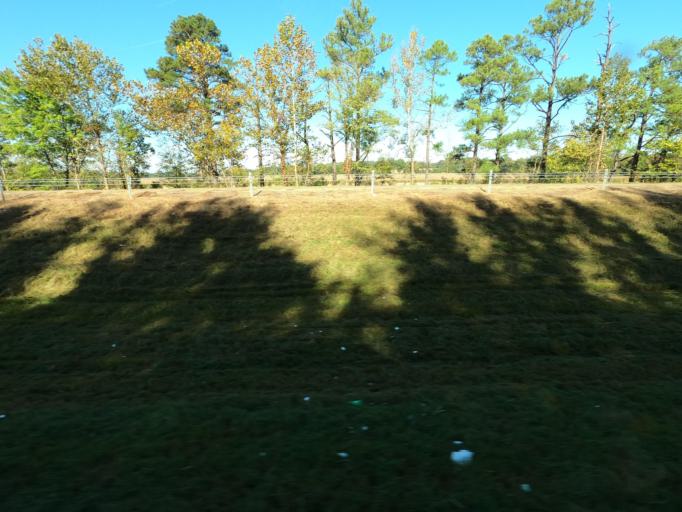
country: US
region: Tennessee
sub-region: Tipton County
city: Brighton
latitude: 35.5004
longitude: -89.7191
